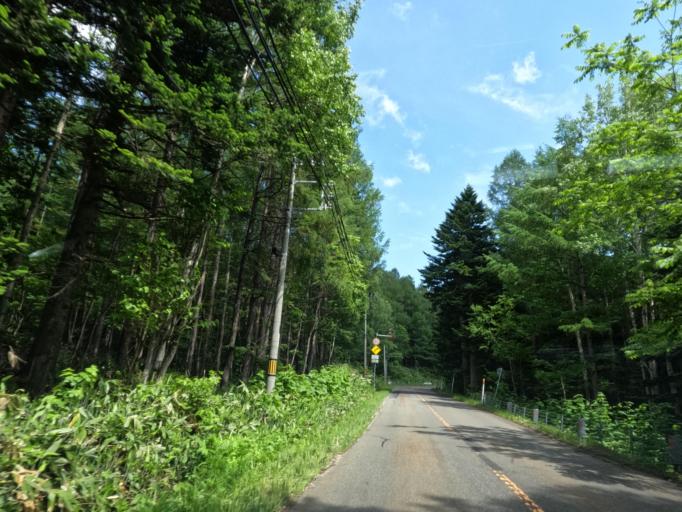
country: JP
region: Hokkaido
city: Takikawa
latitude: 43.5783
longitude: 141.8326
